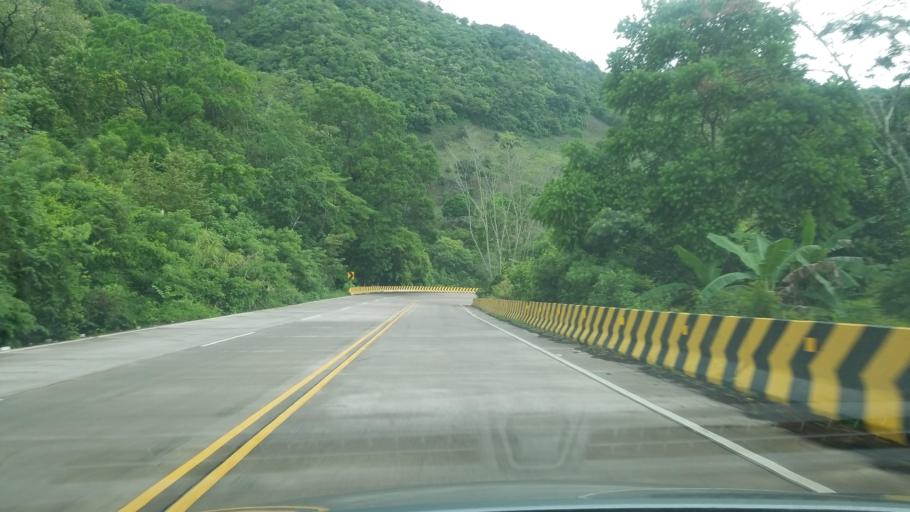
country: HN
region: Copan
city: Copan
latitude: 14.8541
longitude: -89.2162
